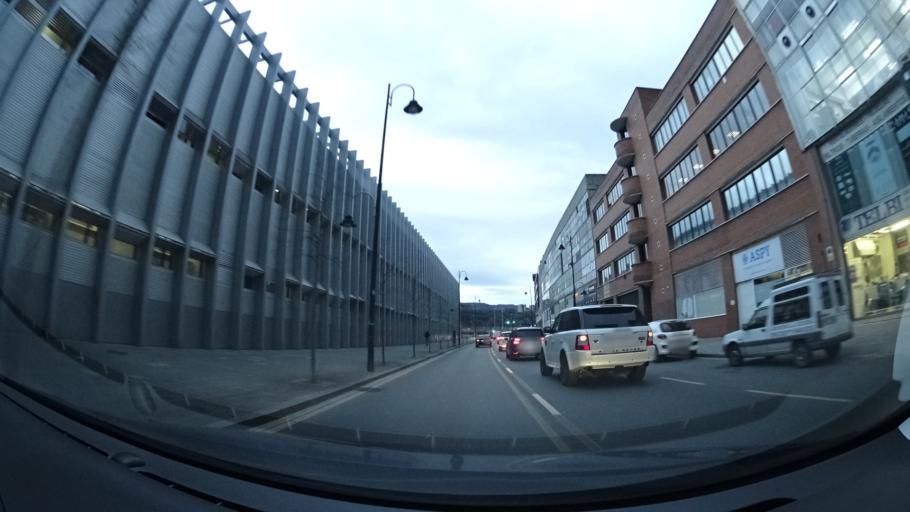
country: ES
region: Basque Country
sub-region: Bizkaia
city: Bilbao
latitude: 43.2681
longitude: -2.9520
